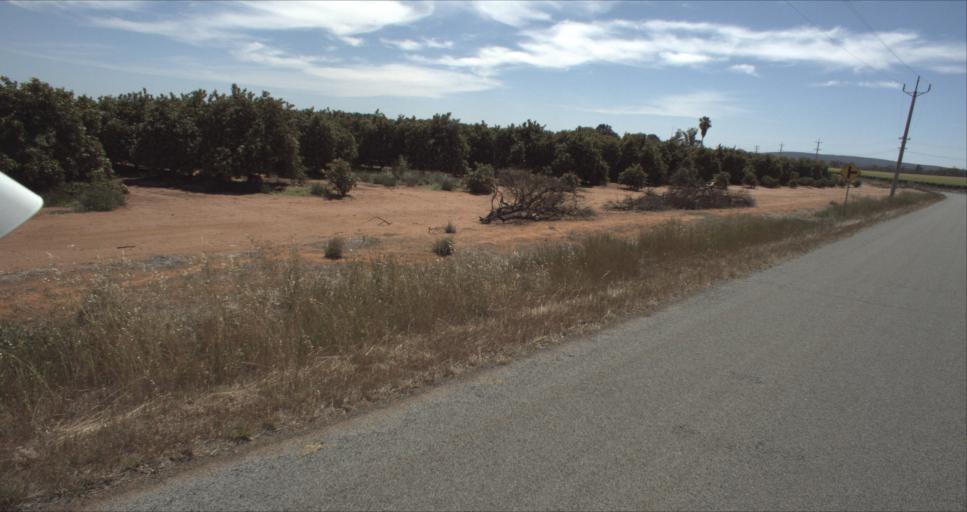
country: AU
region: New South Wales
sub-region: Leeton
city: Leeton
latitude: -34.5662
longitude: 146.4507
